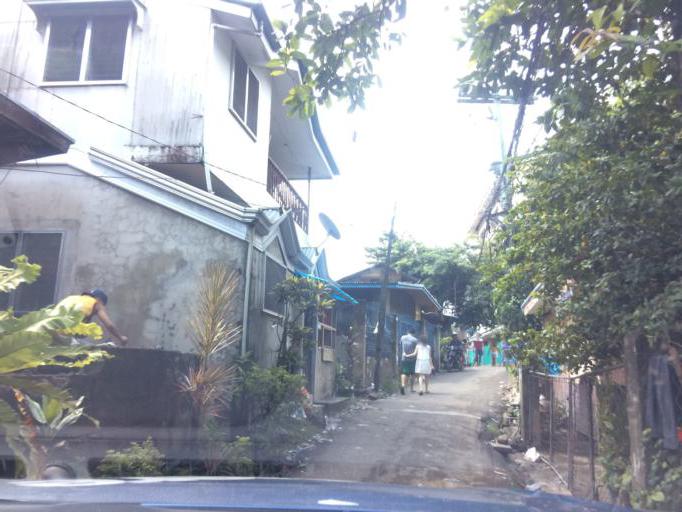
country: PH
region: Central Visayas
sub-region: Province of Cebu
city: Cebu City
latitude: 10.3196
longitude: 123.8970
